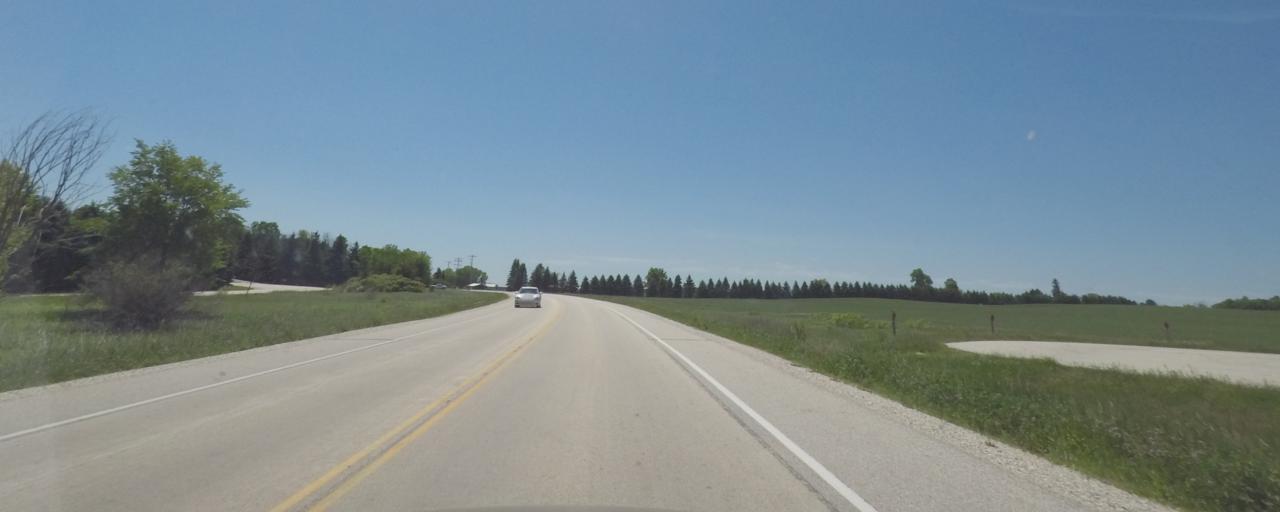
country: US
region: Wisconsin
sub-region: Washington County
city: West Bend
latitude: 43.4940
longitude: -88.1400
